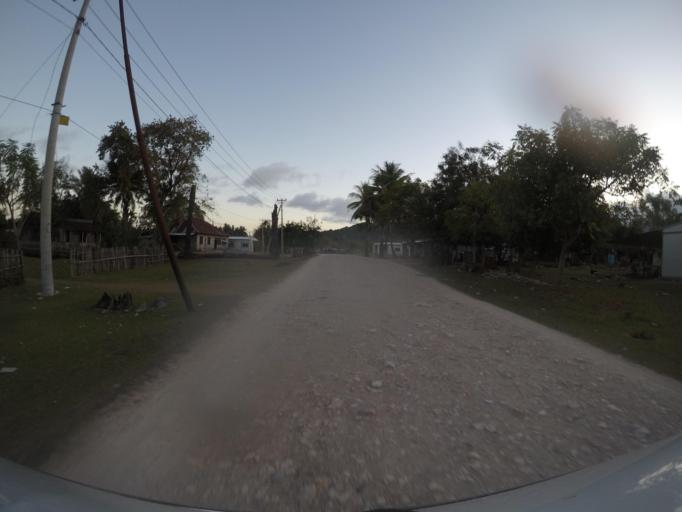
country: TL
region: Viqueque
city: Viqueque
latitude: -8.7766
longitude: 126.6371
